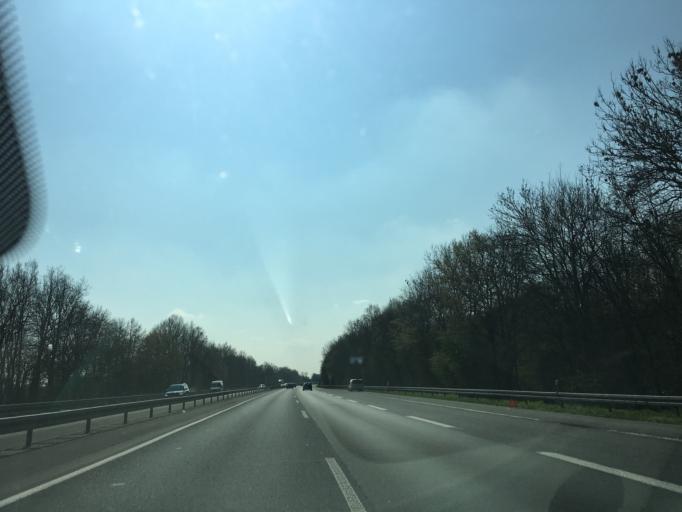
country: DE
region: North Rhine-Westphalia
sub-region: Regierungsbezirk Munster
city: Ascheberg
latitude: 51.7932
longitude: 7.6361
